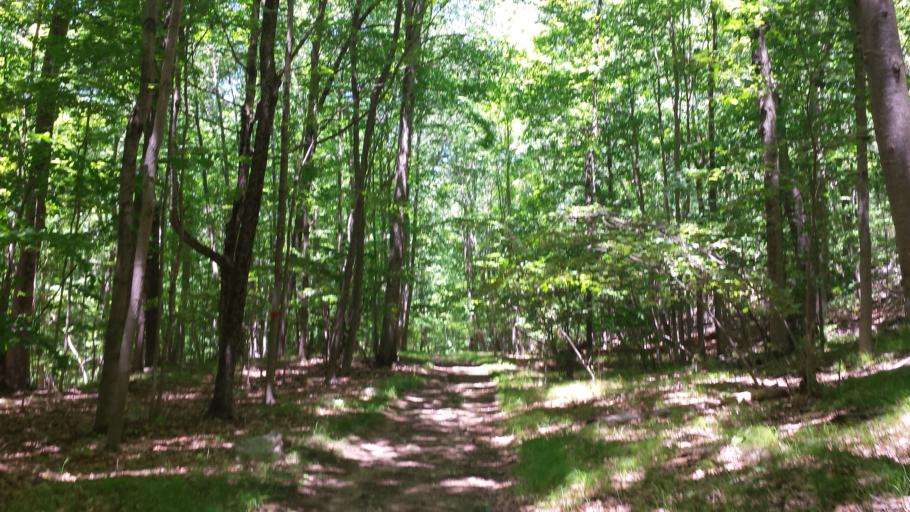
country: US
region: New York
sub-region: Westchester County
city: Pound Ridge
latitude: 41.2515
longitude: -73.5841
